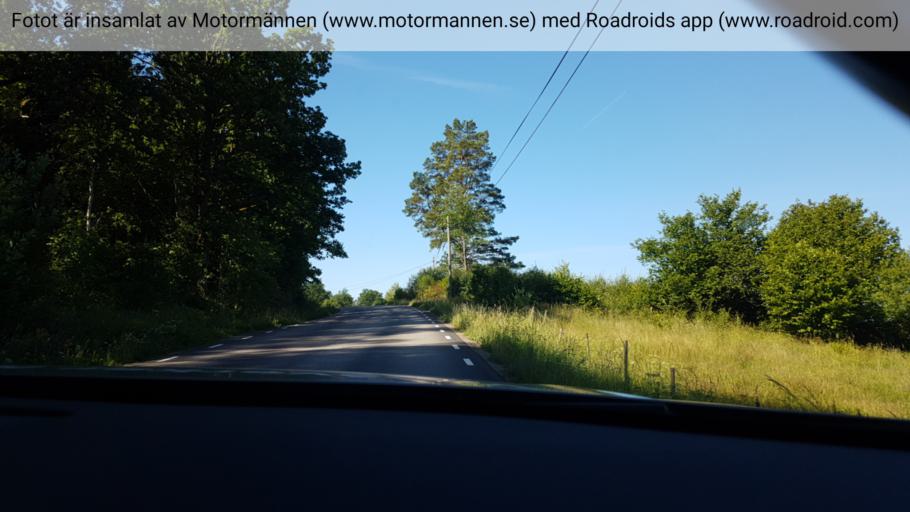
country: SE
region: Vaestra Goetaland
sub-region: Ulricehamns Kommun
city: Ulricehamn
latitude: 57.8528
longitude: 13.3918
